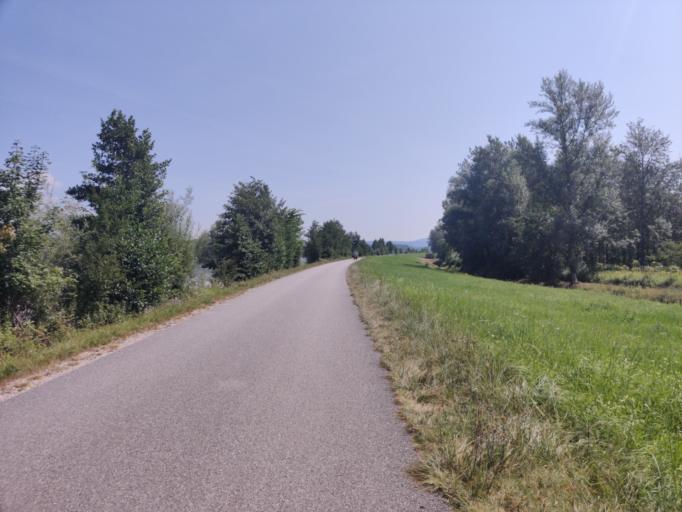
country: AT
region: Upper Austria
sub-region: Politischer Bezirk Urfahr-Umgebung
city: Goldworth
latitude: 48.3145
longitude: 14.0882
